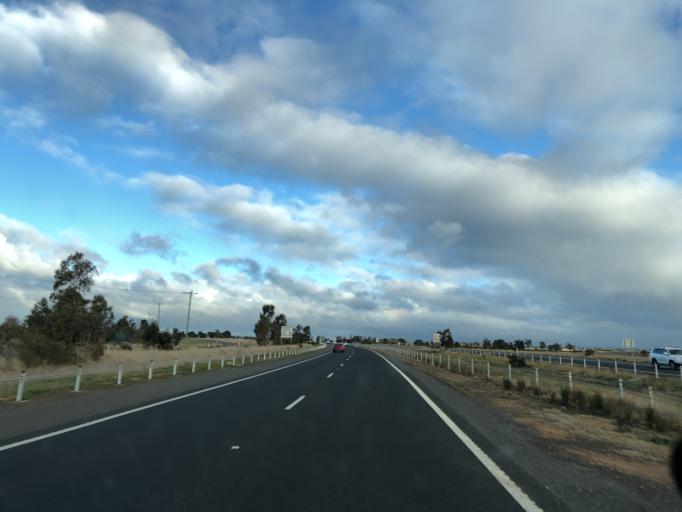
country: AU
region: Victoria
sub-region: Mount Alexander
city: Castlemaine
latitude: -37.1978
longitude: 144.4056
